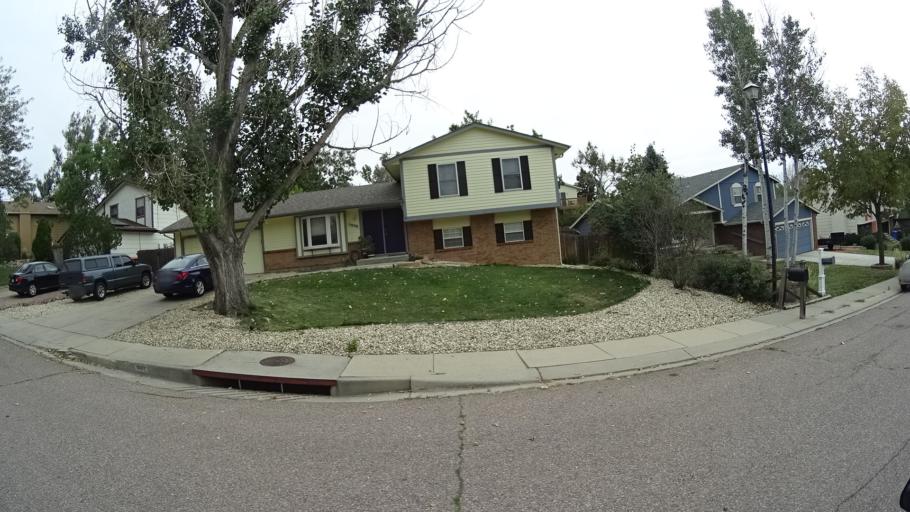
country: US
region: Colorado
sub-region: El Paso County
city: Cimarron Hills
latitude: 38.9036
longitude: -104.7344
